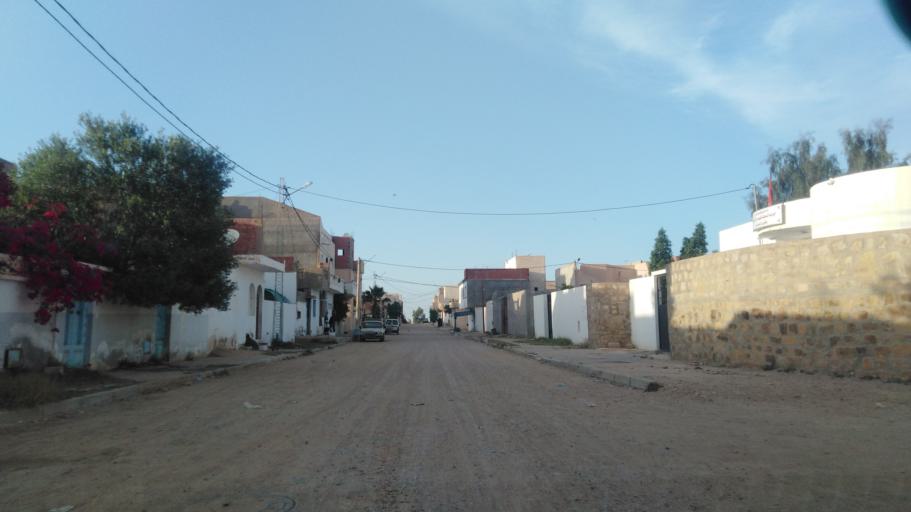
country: TN
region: Tataouine
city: Tataouine
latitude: 32.9408
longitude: 10.4571
